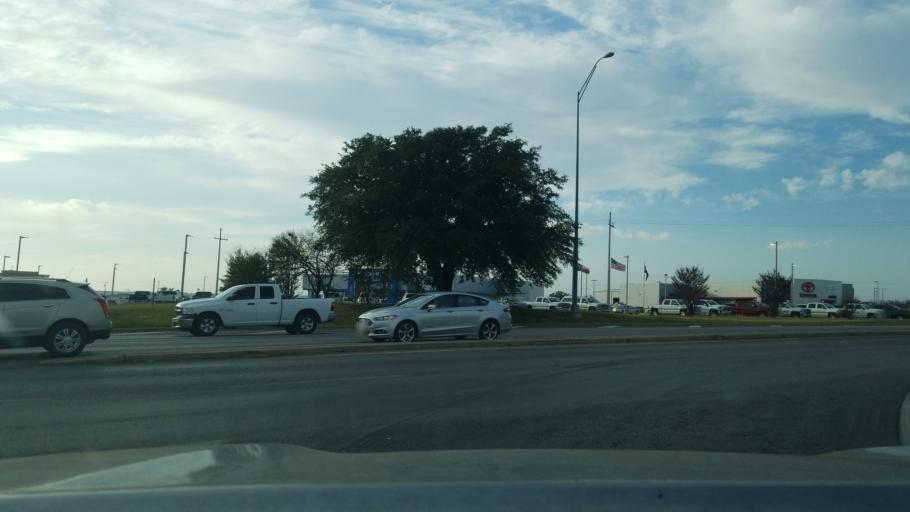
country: US
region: Texas
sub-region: Brown County
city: Early
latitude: 31.7356
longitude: -98.9630
